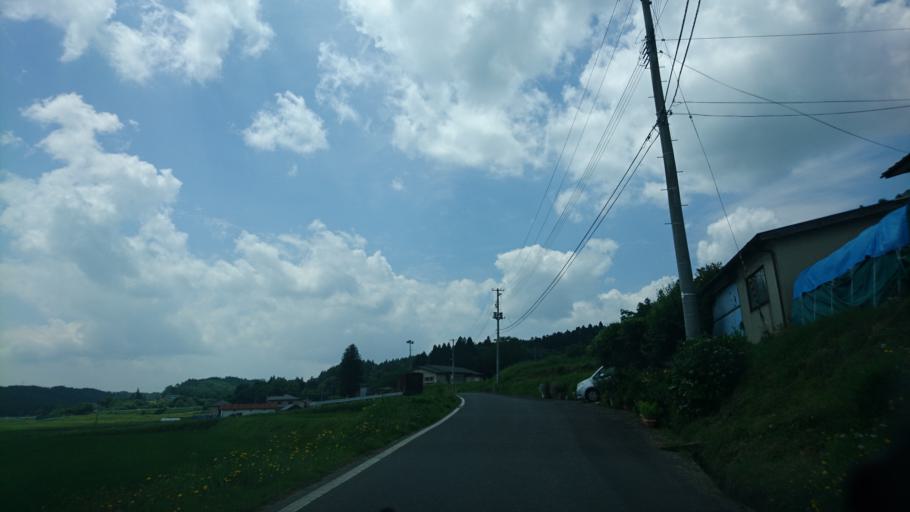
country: JP
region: Iwate
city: Ichinoseki
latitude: 38.9088
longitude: 141.2247
